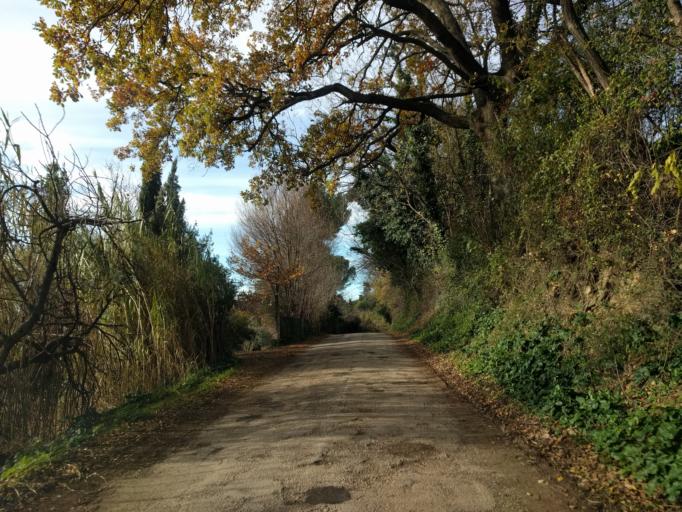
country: IT
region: The Marches
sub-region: Provincia di Pesaro e Urbino
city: Cuccurano
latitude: 43.8075
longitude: 12.9551
